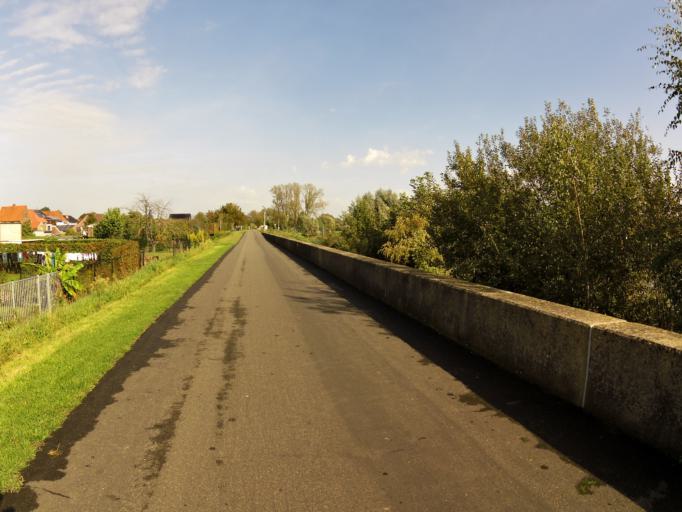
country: NL
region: Limburg
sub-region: Gemeente Meerssen
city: Meerssen
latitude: 50.9284
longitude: 5.7303
